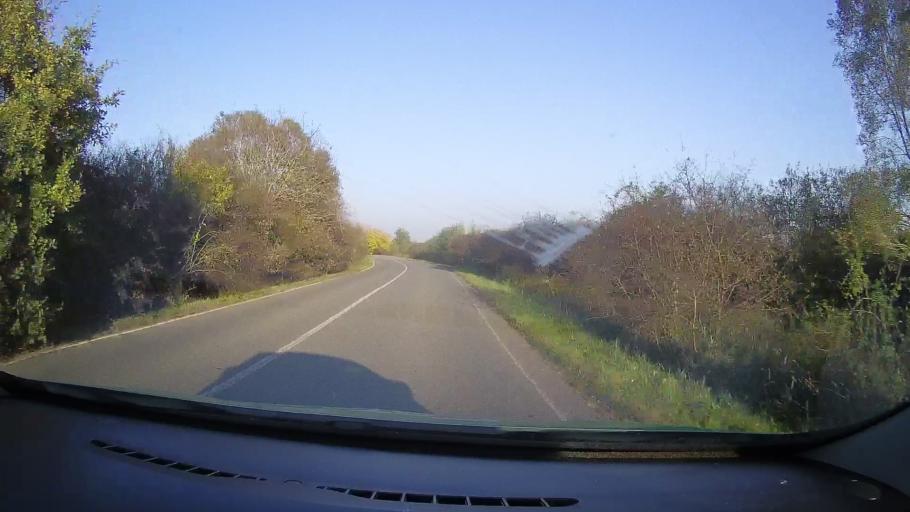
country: RO
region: Arad
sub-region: Comuna Silindia
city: Silindia
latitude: 46.3356
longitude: 21.8769
